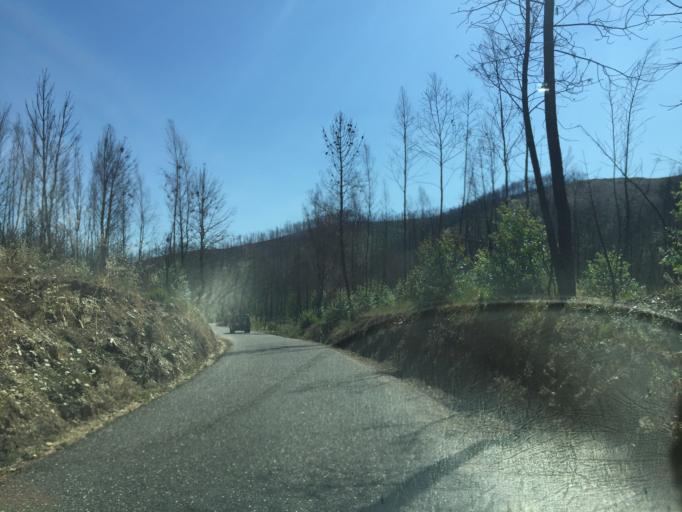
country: PT
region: Coimbra
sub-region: Pampilhosa da Serra
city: Pampilhosa da Serra
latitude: 40.0229
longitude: -7.8363
